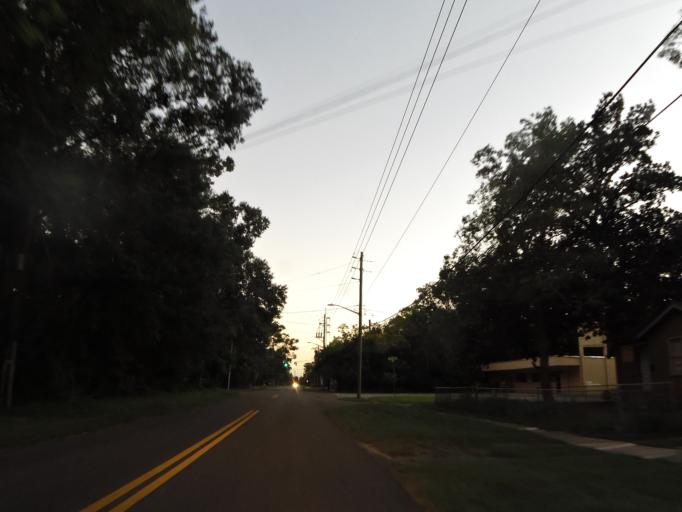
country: US
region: Florida
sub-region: Duval County
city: Jacksonville
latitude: 30.3045
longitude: -81.7222
